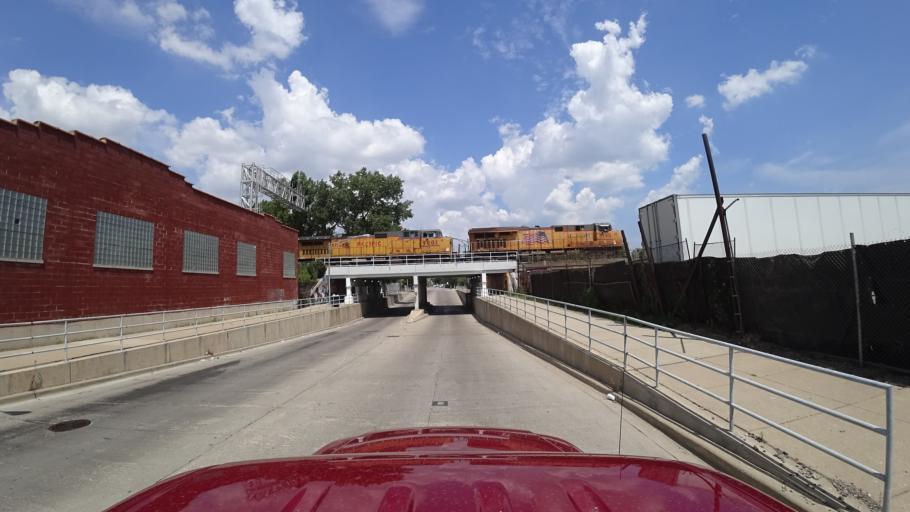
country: US
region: Illinois
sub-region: Cook County
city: Chicago
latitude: 41.8212
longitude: -87.6410
